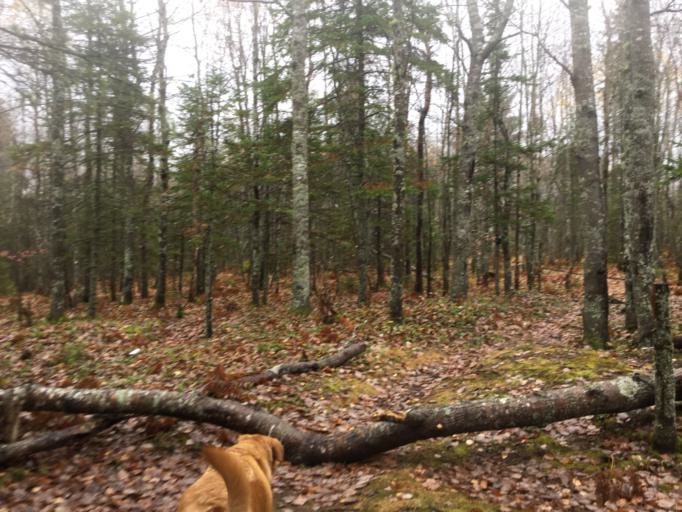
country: CA
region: Nova Scotia
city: New Glasgow
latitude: 45.5544
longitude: -62.6790
